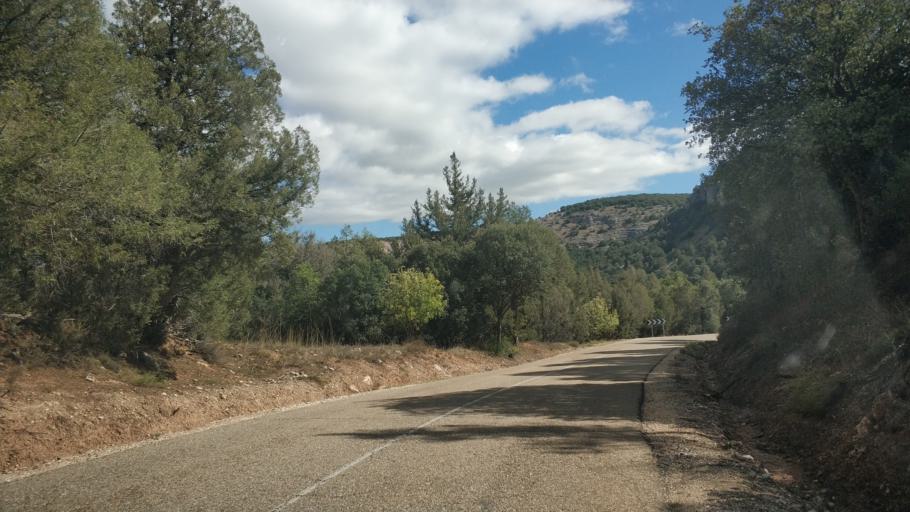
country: ES
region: Castille and Leon
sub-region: Provincia de Burgos
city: Retuerta
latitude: 42.0438
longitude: -3.4745
